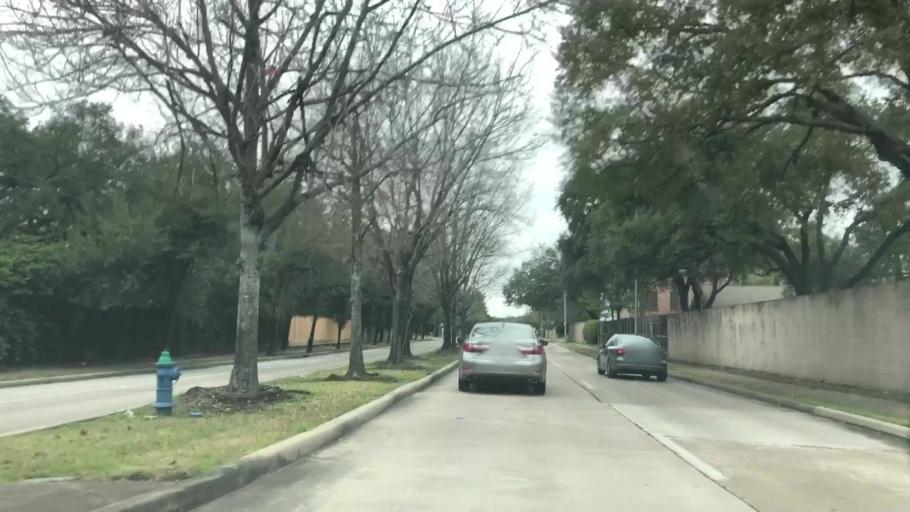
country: US
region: Texas
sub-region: Harris County
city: Hunters Creek Village
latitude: 29.7569
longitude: -95.4932
